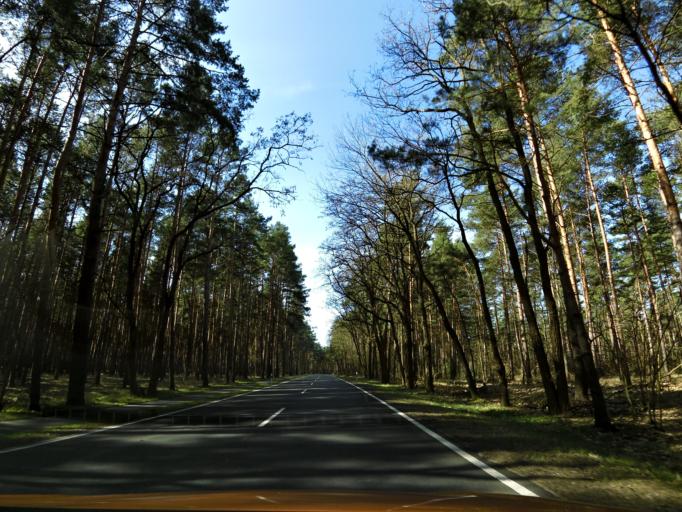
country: DE
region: Brandenburg
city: Borkheide
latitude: 52.2139
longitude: 12.8917
